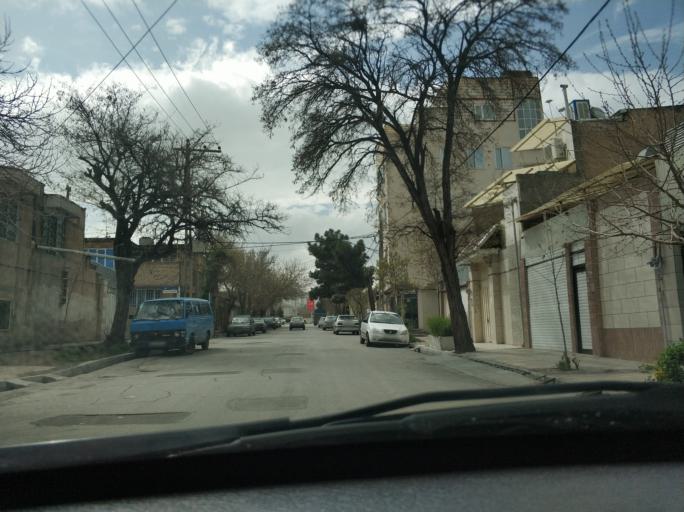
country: IR
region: Razavi Khorasan
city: Mashhad
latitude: 36.2732
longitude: 59.5707
